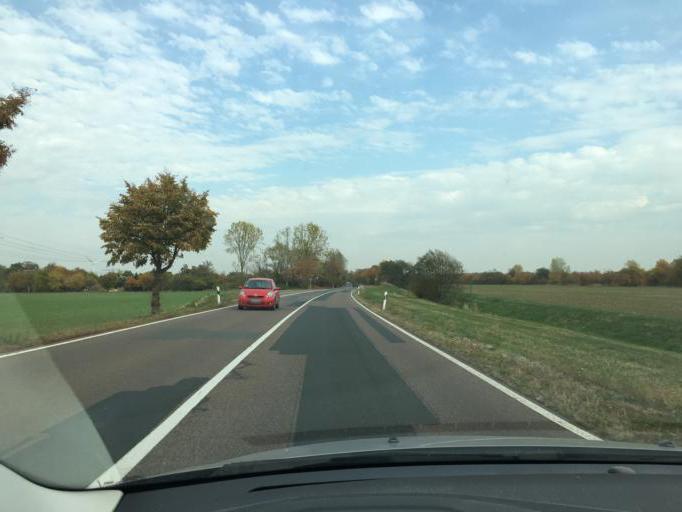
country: DE
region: Saxony
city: Zwochau
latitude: 51.4887
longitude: 12.2715
